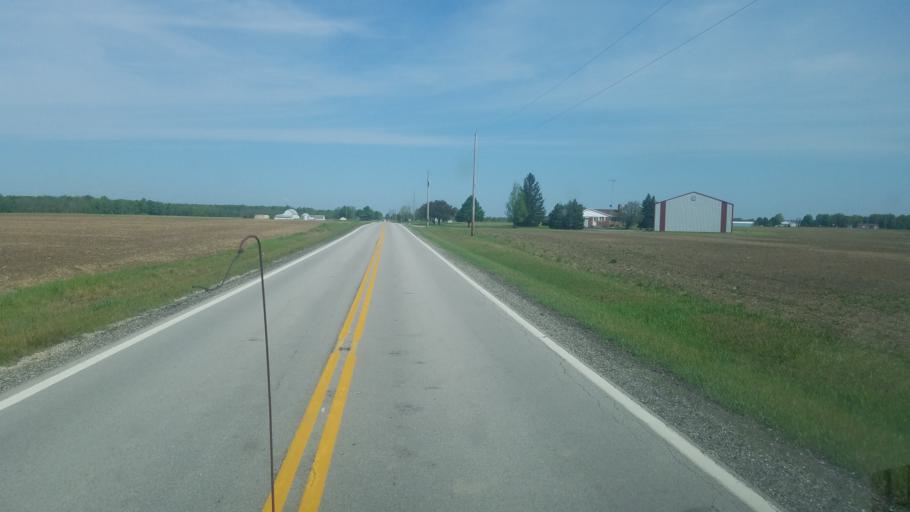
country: US
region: Ohio
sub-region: Seneca County
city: Tiffin
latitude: 40.9644
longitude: -83.0750
